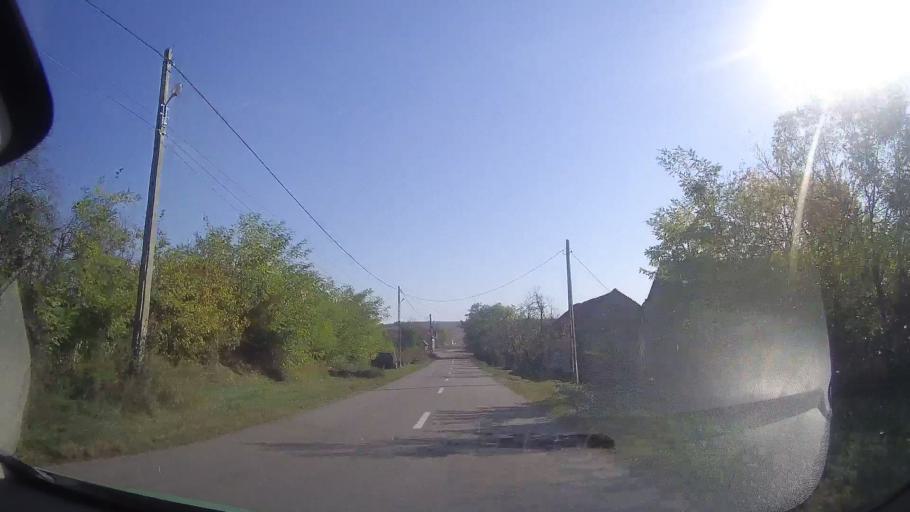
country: RO
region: Timis
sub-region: Comuna Secas
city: Secas
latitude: 45.8450
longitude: 21.7911
